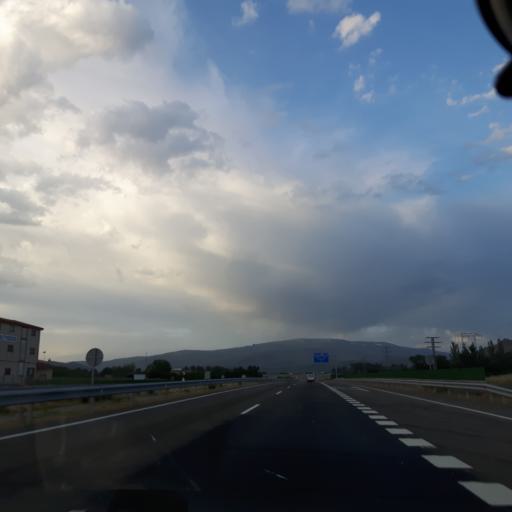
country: ES
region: Castille and Leon
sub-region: Provincia de Salamanca
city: Nava de Bejar
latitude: 40.4946
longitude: -5.6760
